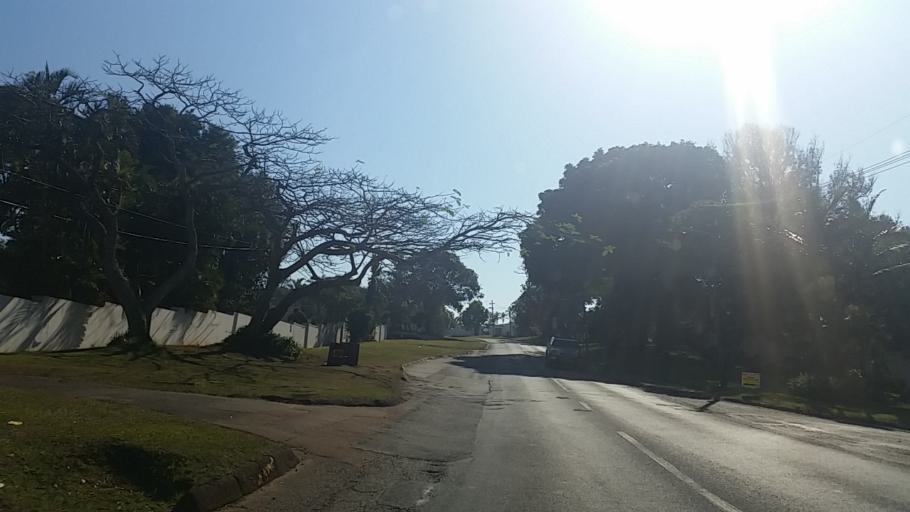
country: ZA
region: KwaZulu-Natal
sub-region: eThekwini Metropolitan Municipality
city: Berea
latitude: -29.8314
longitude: 30.8979
